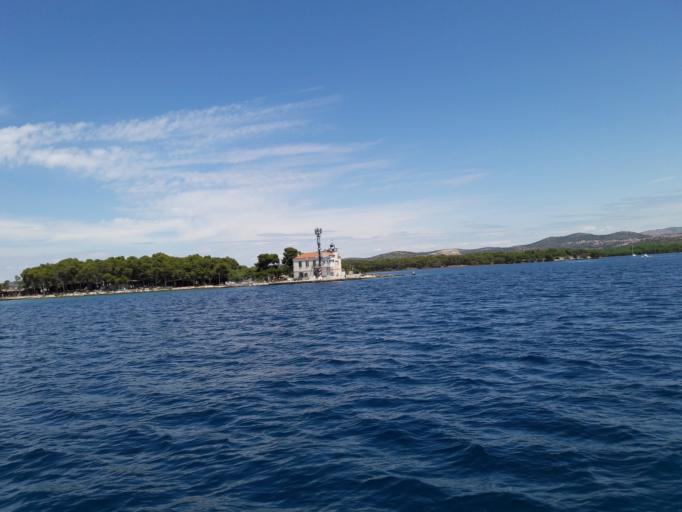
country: HR
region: Sibensko-Kniniska
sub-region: Grad Sibenik
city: Sibenik
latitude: 43.7201
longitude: 15.8494
